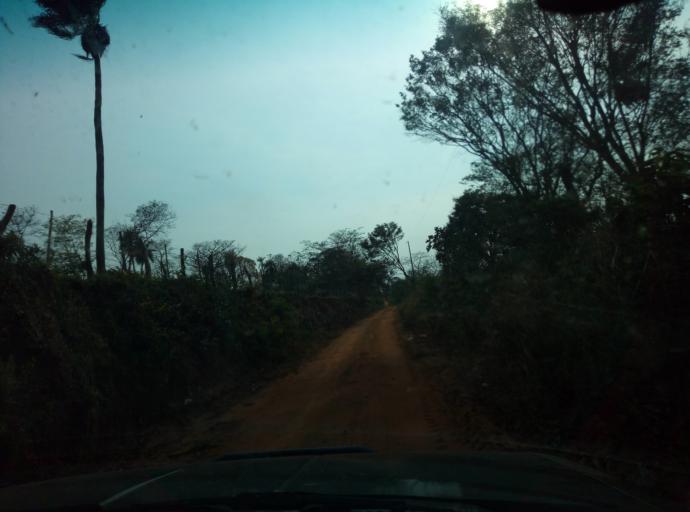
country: PY
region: Caaguazu
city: San Joaquin
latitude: -25.1509
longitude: -56.1033
